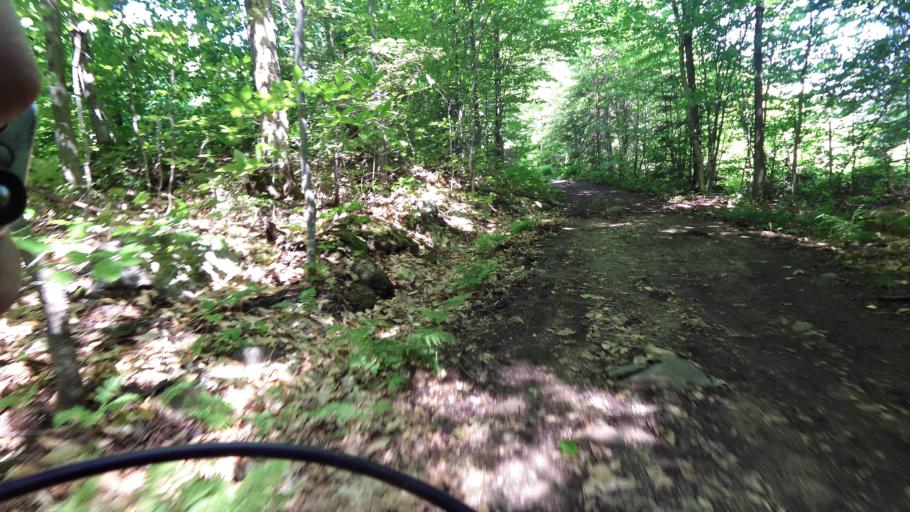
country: CA
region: Quebec
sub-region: Outaouais
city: Wakefield
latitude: 45.5437
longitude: -75.8918
